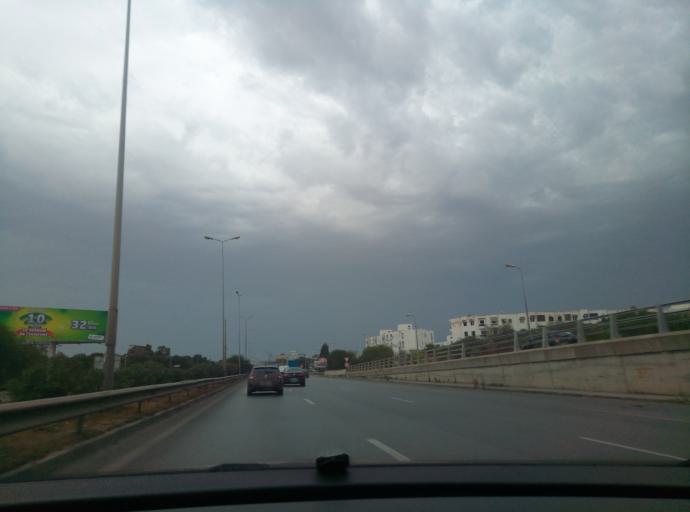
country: TN
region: Bin 'Arus
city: Ben Arous
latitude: 36.7455
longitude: 10.2107
